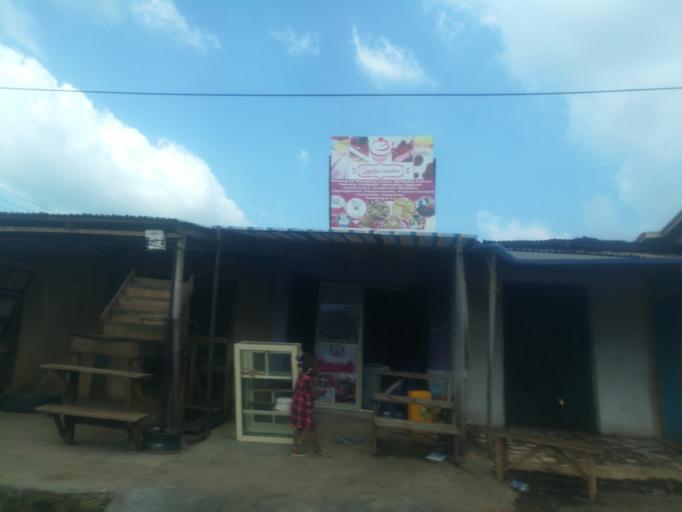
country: NG
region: Oyo
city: Ibadan
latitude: 7.4274
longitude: 3.8403
